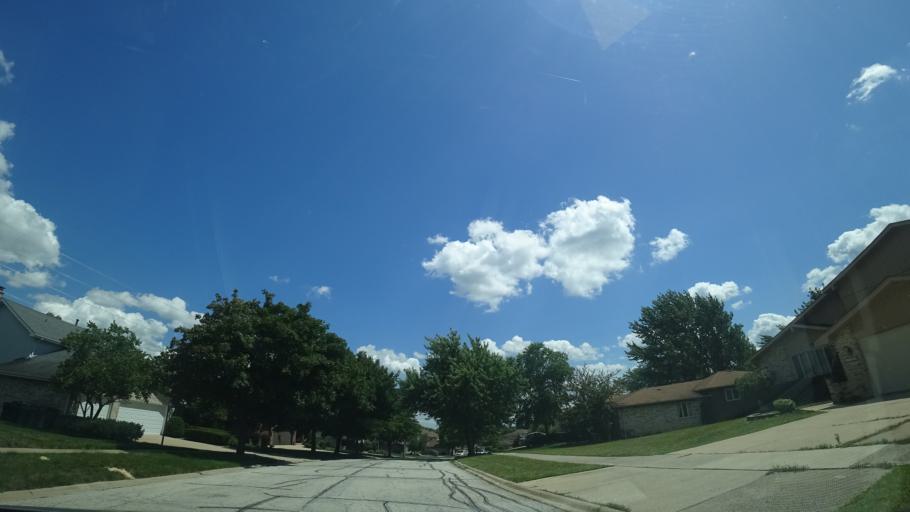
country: US
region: Illinois
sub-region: Will County
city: Homer Glen
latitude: 41.5774
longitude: -87.9011
